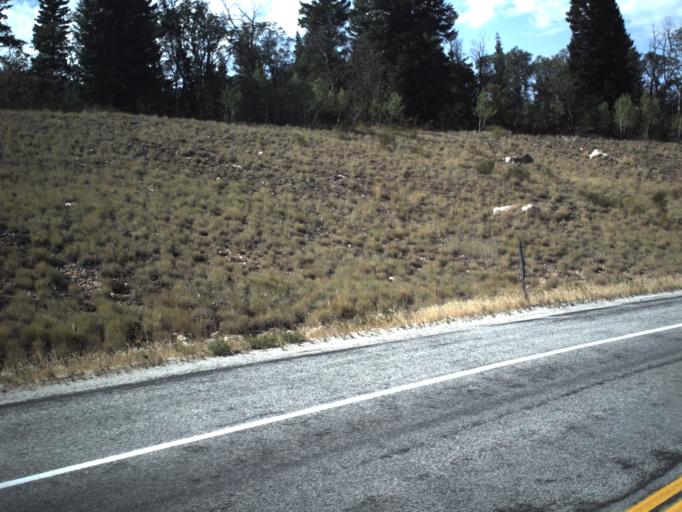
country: US
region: Utah
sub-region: Morgan County
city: Mountain Green
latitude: 41.2180
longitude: -111.8517
